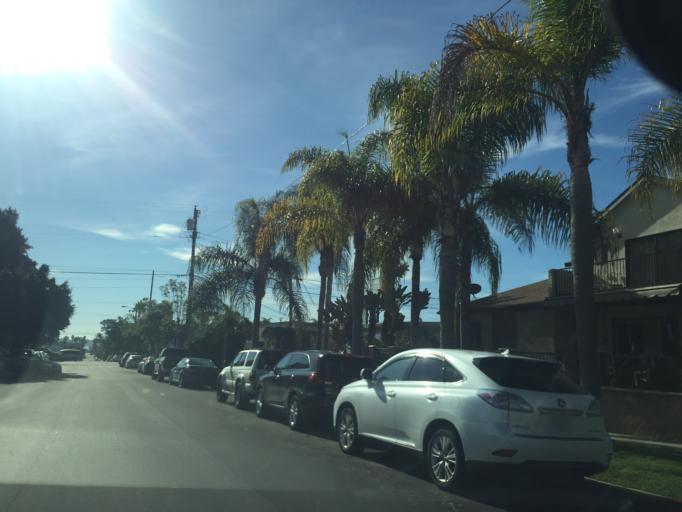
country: US
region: California
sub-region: San Diego County
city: La Jolla
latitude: 32.8023
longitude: -117.2338
